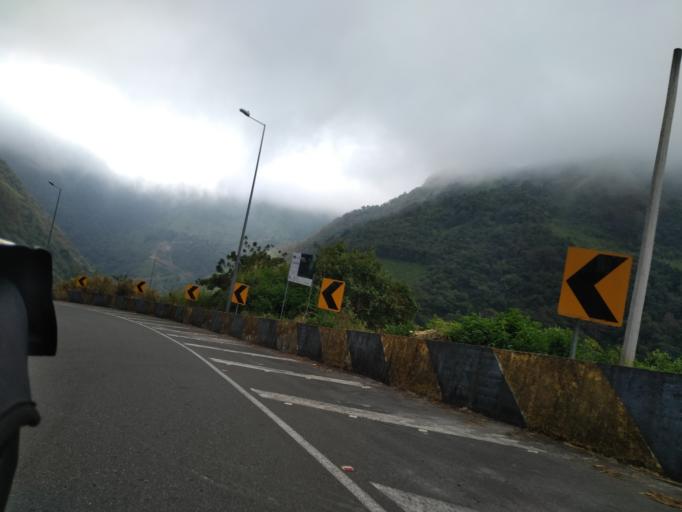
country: EC
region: Cotopaxi
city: La Mana
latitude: -0.8942
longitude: -79.0560
